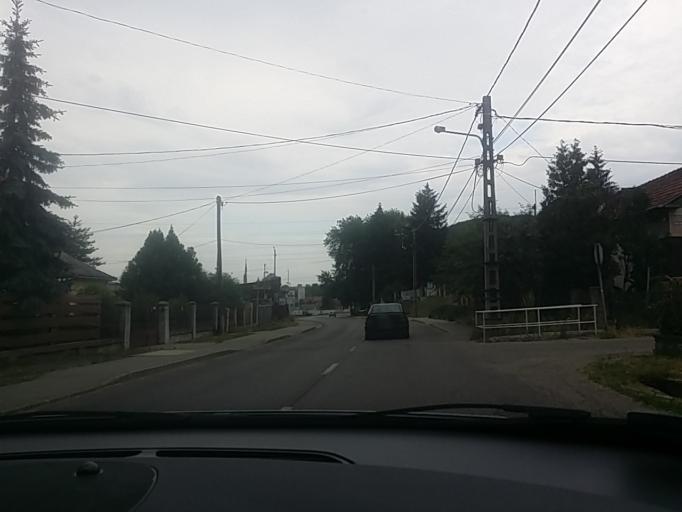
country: HU
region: Borsod-Abauj-Zemplen
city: Arlo
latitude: 48.2129
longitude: 20.2680
